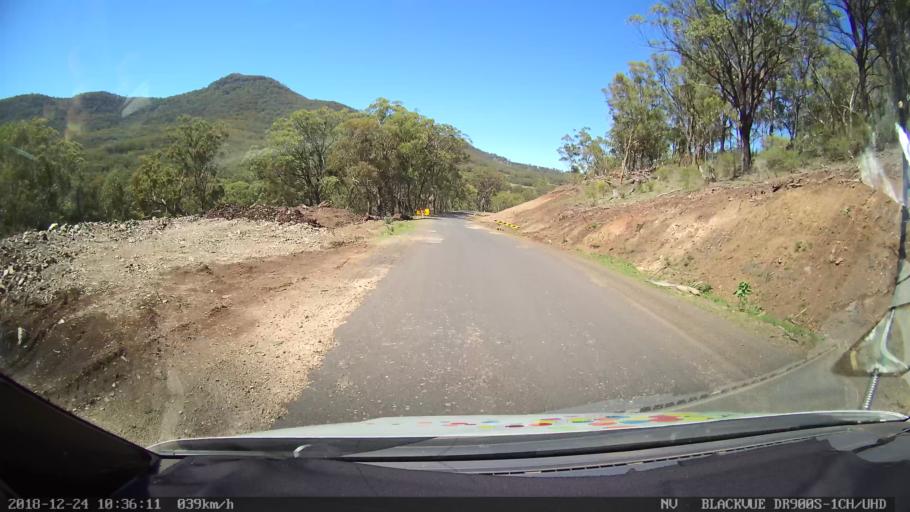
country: AU
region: New South Wales
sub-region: Upper Hunter Shire
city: Merriwa
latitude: -31.8430
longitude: 150.5006
